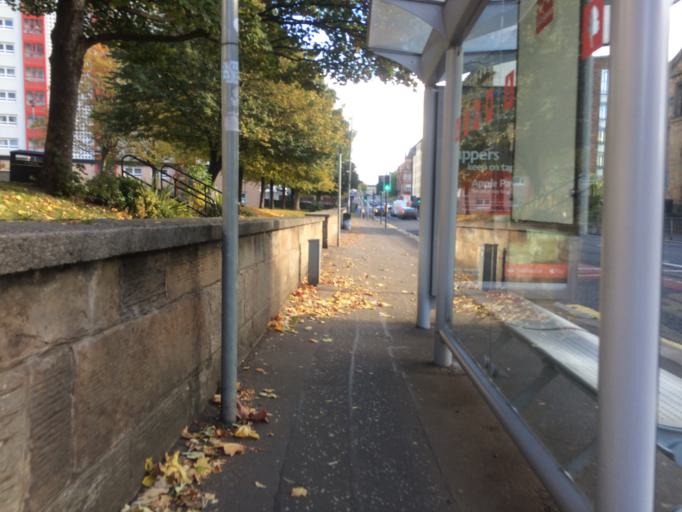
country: GB
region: Scotland
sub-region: Glasgow City
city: Glasgow
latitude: 55.8599
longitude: -4.2357
